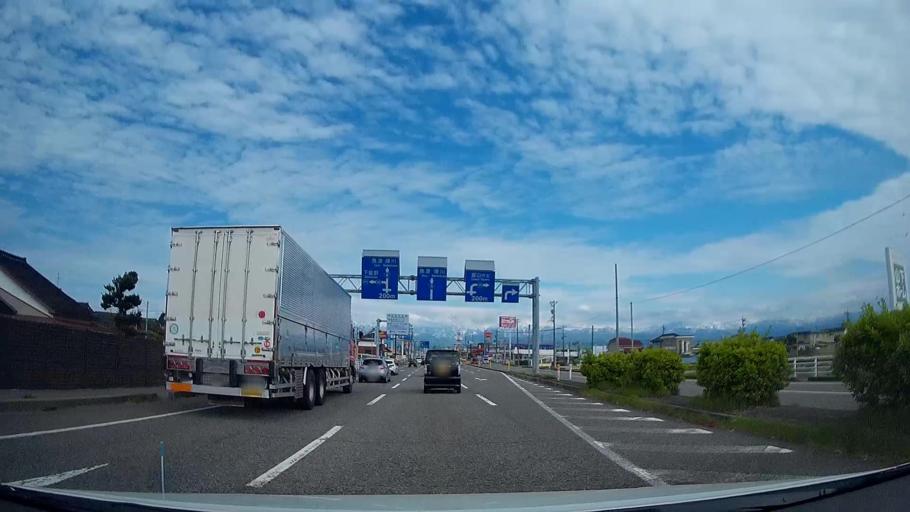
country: JP
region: Toyama
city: Toyama-shi
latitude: 36.7222
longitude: 137.2474
